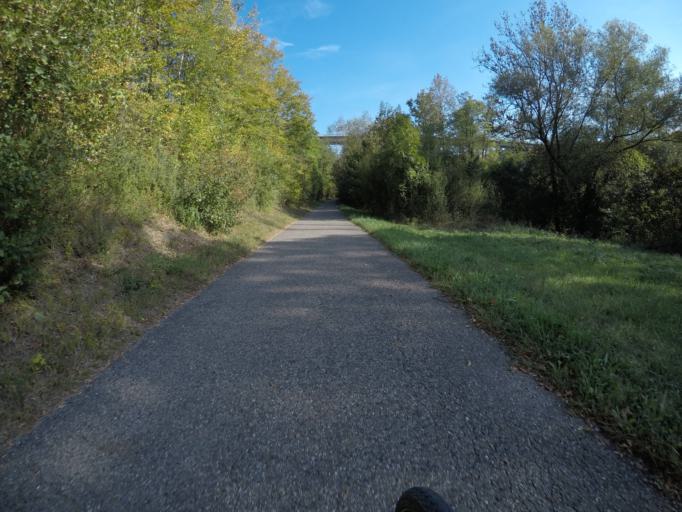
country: DE
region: Baden-Wuerttemberg
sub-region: Regierungsbezirk Stuttgart
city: Schlaitdorf
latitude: 48.6215
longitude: 9.2223
